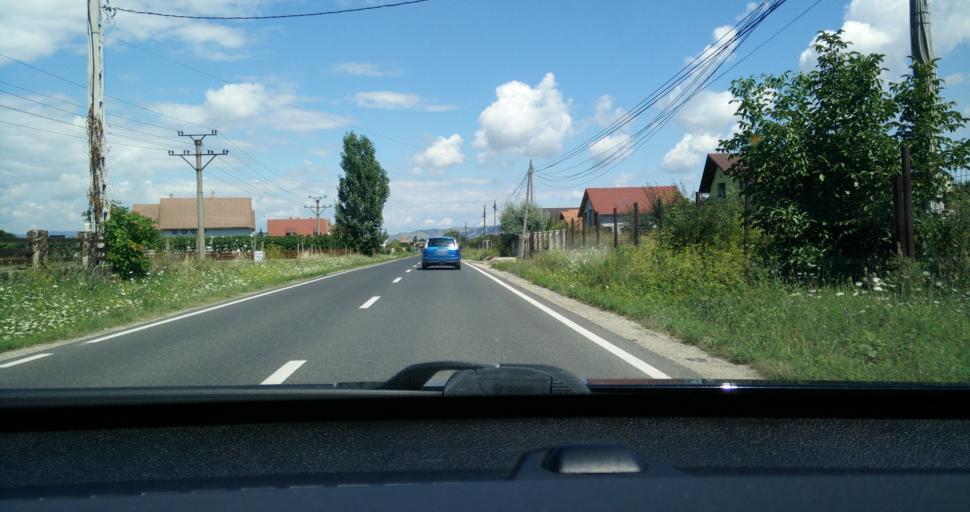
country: RO
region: Alba
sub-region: Municipiul Sebes
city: Petresti
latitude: 45.9132
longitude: 23.5545
